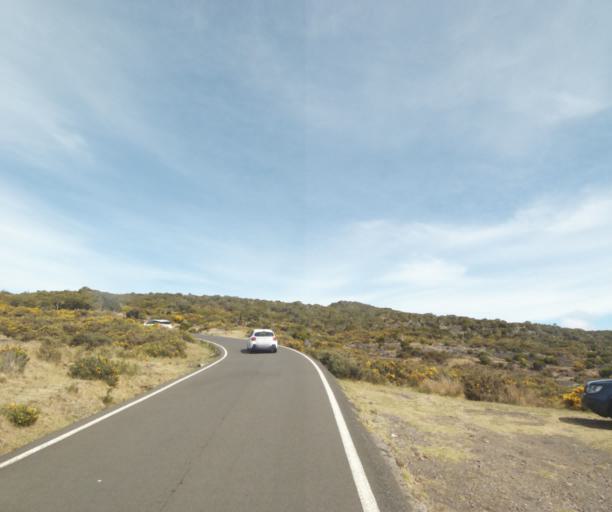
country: RE
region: Reunion
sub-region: Reunion
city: Trois-Bassins
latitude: -21.0717
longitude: 55.3867
